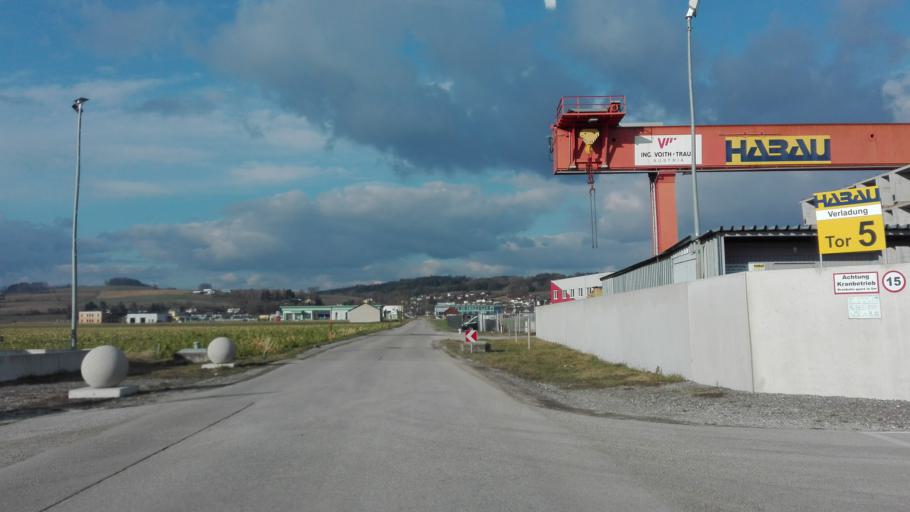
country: AT
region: Upper Austria
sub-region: Politischer Bezirk Perg
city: Perg
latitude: 48.2404
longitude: 14.6204
